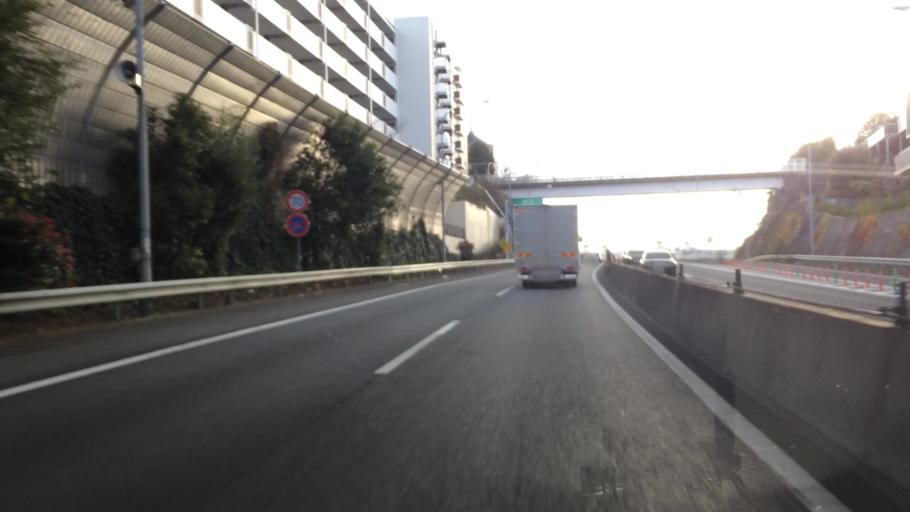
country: JP
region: Kanagawa
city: Yokohama
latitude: 35.4338
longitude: 139.5540
